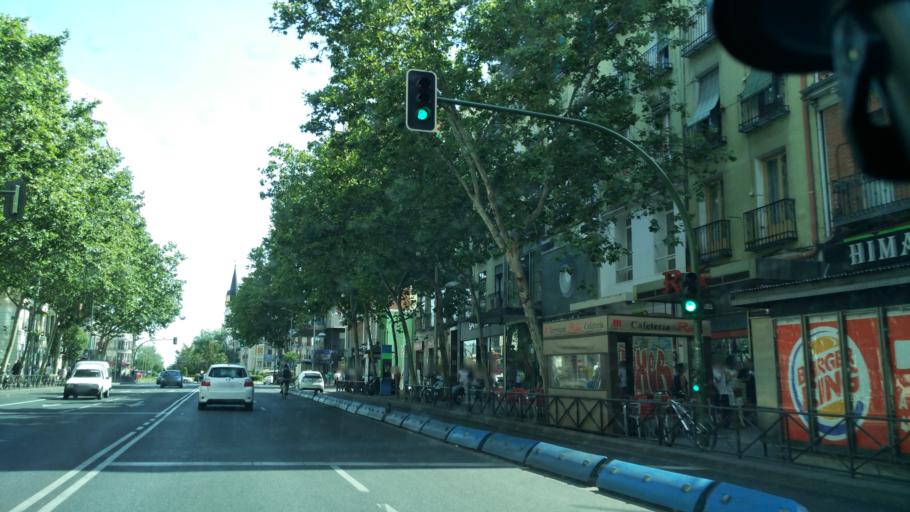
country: ES
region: Madrid
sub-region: Provincia de Madrid
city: Chamberi
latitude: 40.4486
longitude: -3.7037
